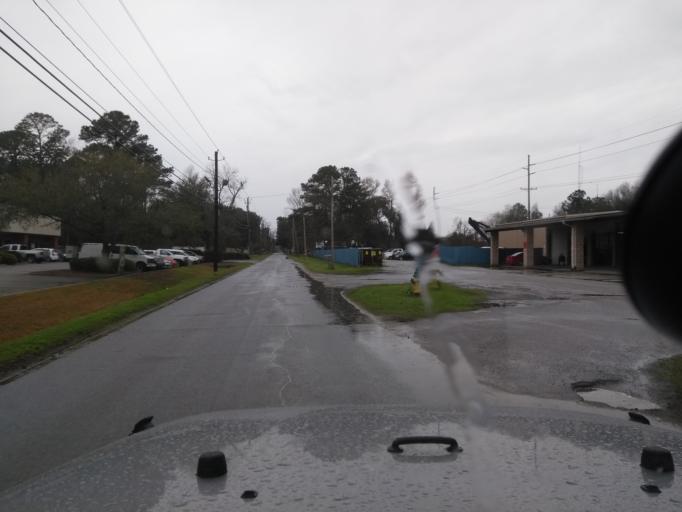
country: US
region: Georgia
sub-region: Chatham County
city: Garden City
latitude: 32.0914
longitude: -81.1595
